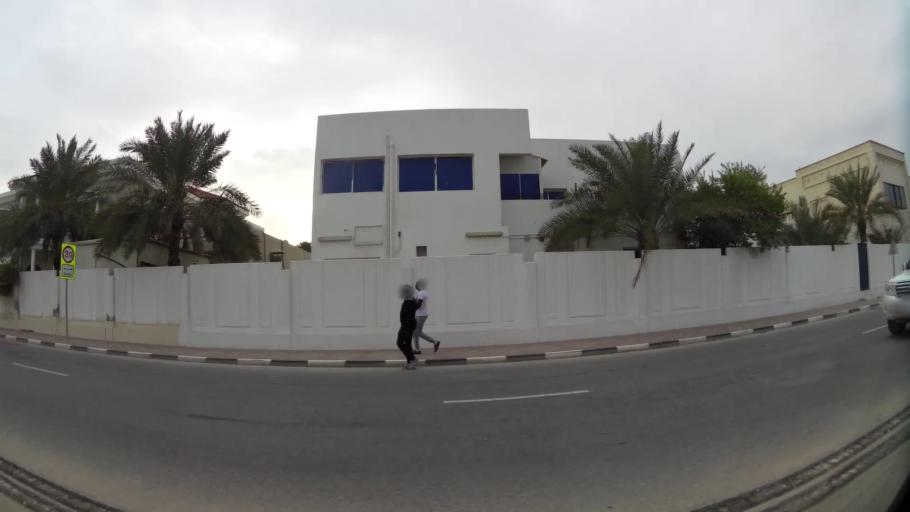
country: QA
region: Baladiyat ad Dawhah
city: Doha
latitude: 25.3302
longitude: 51.5108
